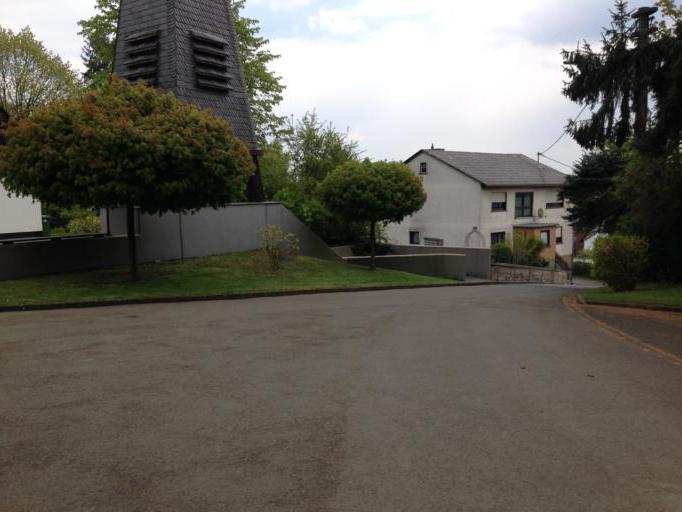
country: DE
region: Hesse
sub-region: Regierungsbezirk Giessen
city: Grunberg
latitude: 50.6124
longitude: 8.9852
